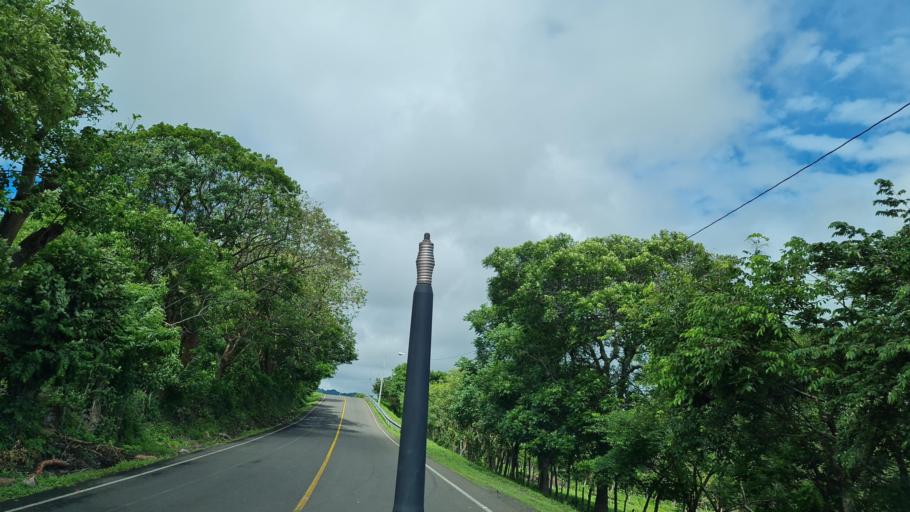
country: NI
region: Boaco
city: San Jose de los Remates
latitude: 12.6113
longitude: -85.8941
